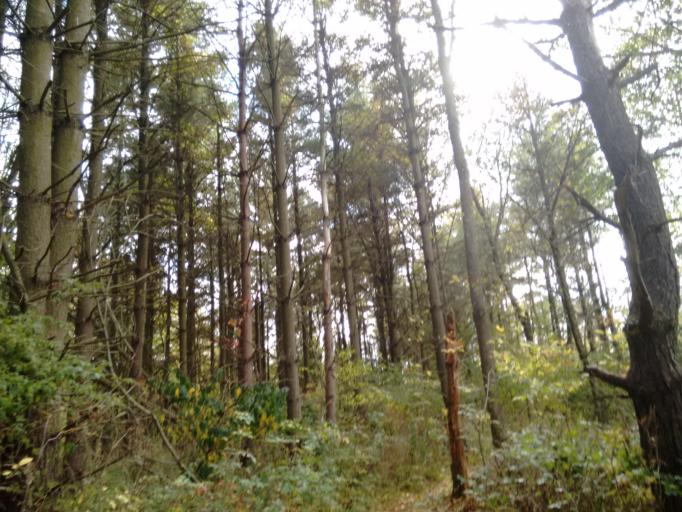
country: CA
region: Ontario
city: St. Thomas
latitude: 42.7450
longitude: -81.2054
